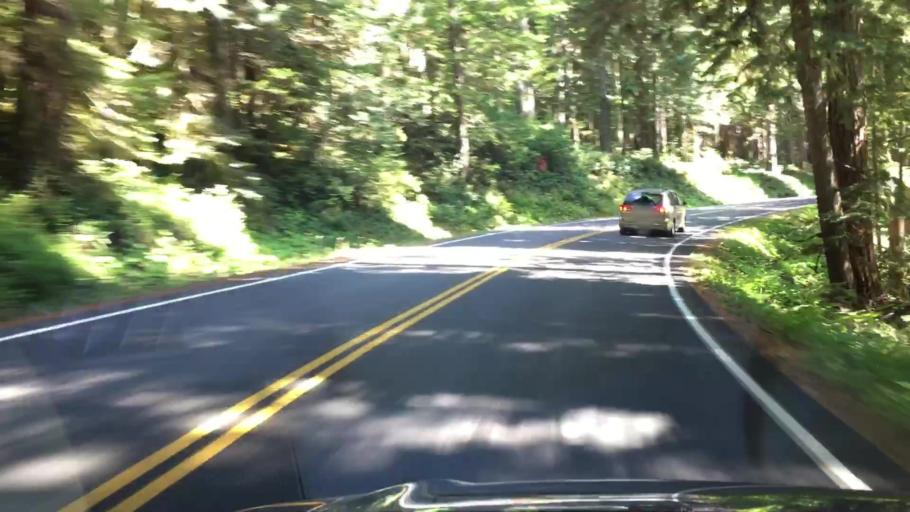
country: US
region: Washington
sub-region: Pierce County
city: Eatonville
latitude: 46.7316
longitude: -121.8345
